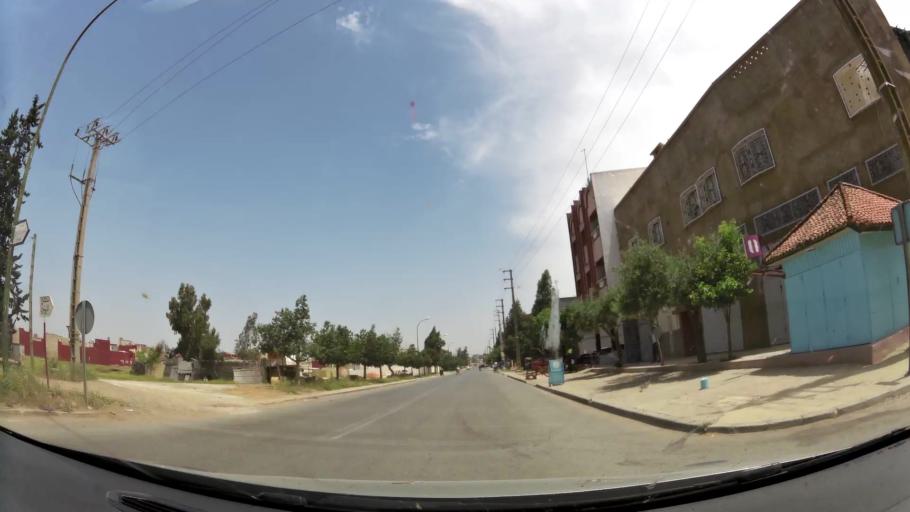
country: MA
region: Rabat-Sale-Zemmour-Zaer
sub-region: Khemisset
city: Khemisset
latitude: 33.8210
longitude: -6.0800
